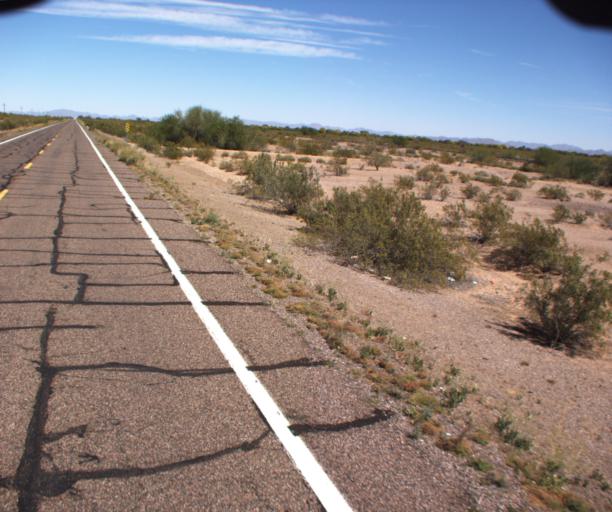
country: US
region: Arizona
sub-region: Maricopa County
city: Gila Bend
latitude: 32.8221
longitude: -112.7873
